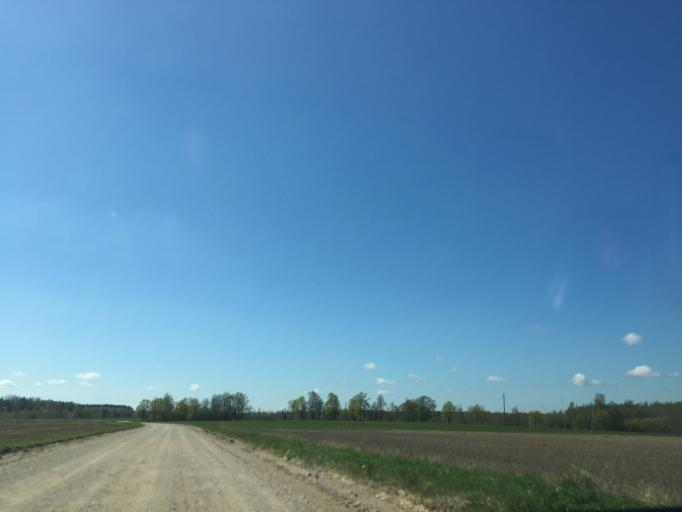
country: LV
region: Smiltene
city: Smiltene
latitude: 57.5548
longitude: 25.8647
